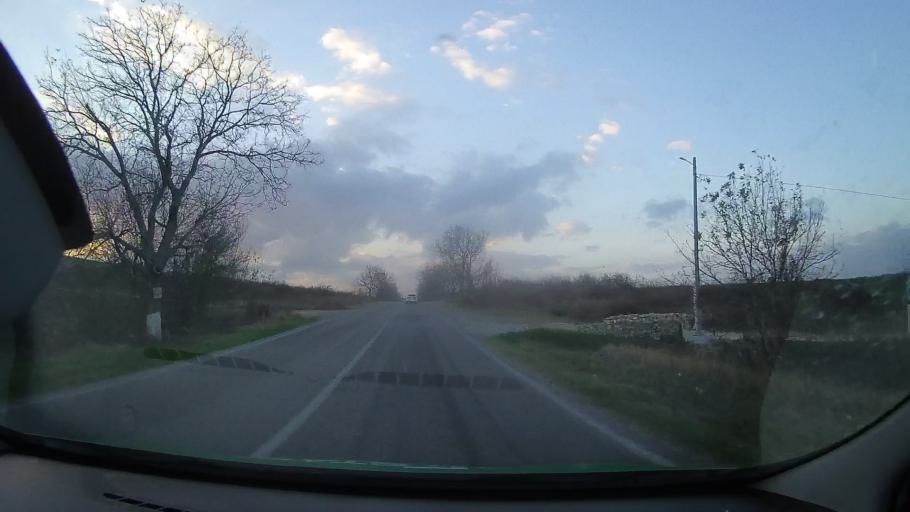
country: RO
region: Constanta
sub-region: Comuna Lipnita
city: Lipnita
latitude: 44.0945
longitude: 27.6409
